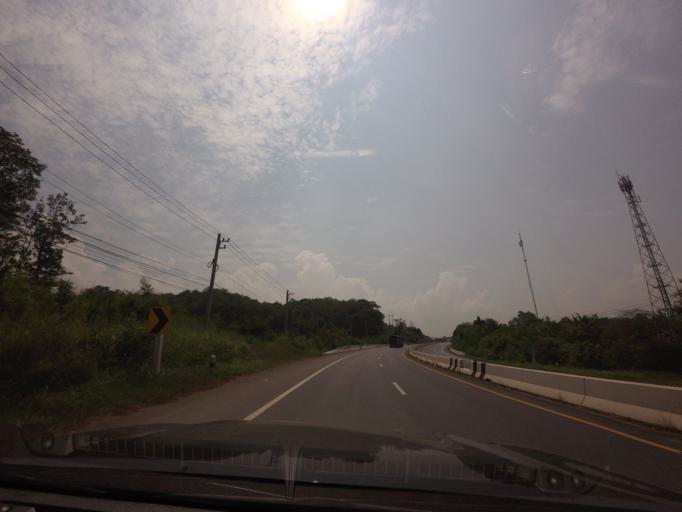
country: TH
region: Phrae
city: Den Chai
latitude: 17.9370
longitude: 100.0614
